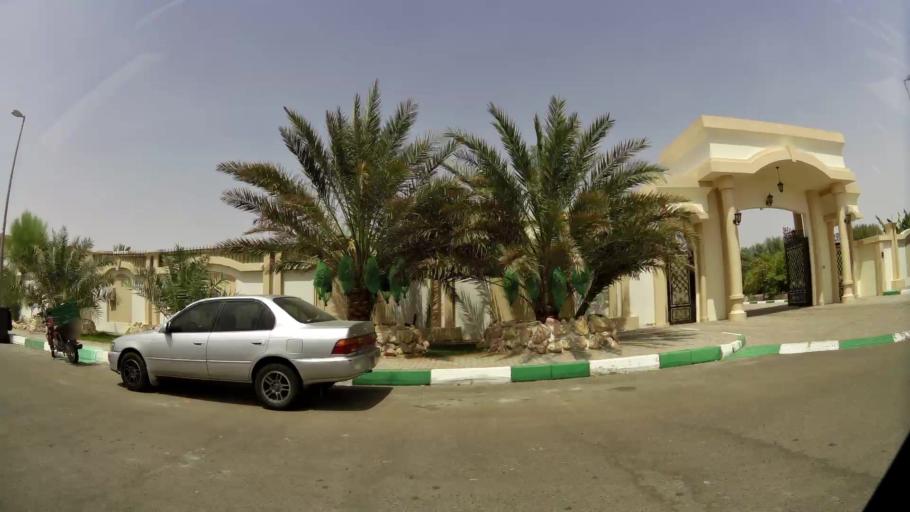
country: AE
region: Abu Dhabi
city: Al Ain
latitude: 24.1444
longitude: 55.6411
